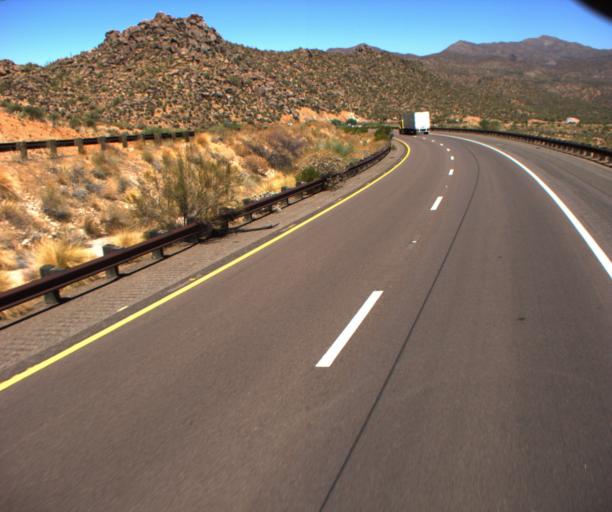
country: US
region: Arizona
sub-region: Maricopa County
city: Rio Verde
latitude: 33.7095
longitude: -111.5063
